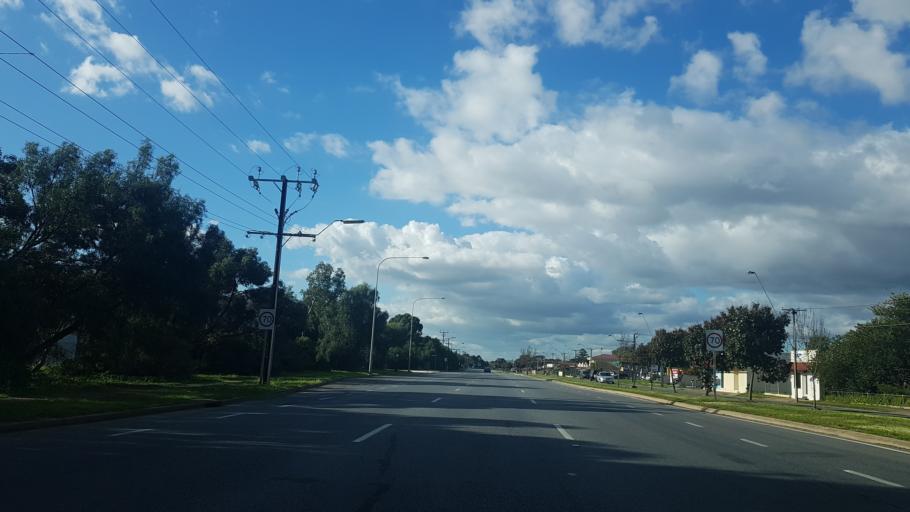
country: AU
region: South Australia
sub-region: Salisbury
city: Ingle Farm
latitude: -34.8315
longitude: 138.6120
